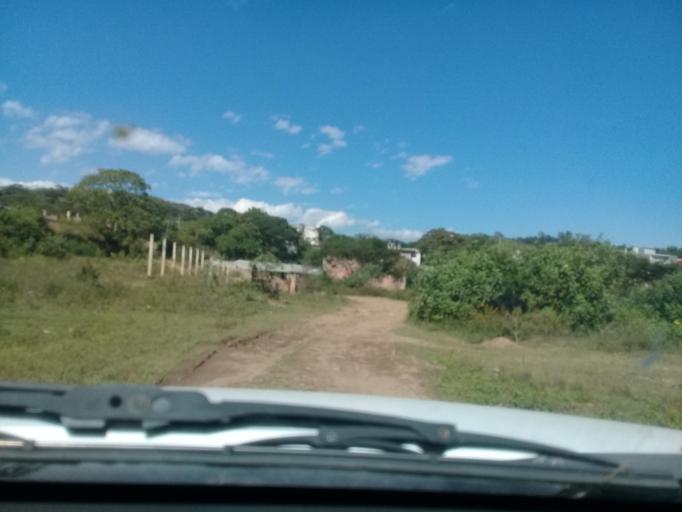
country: MX
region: Veracruz
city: El Castillo
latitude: 19.5505
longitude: -96.8552
